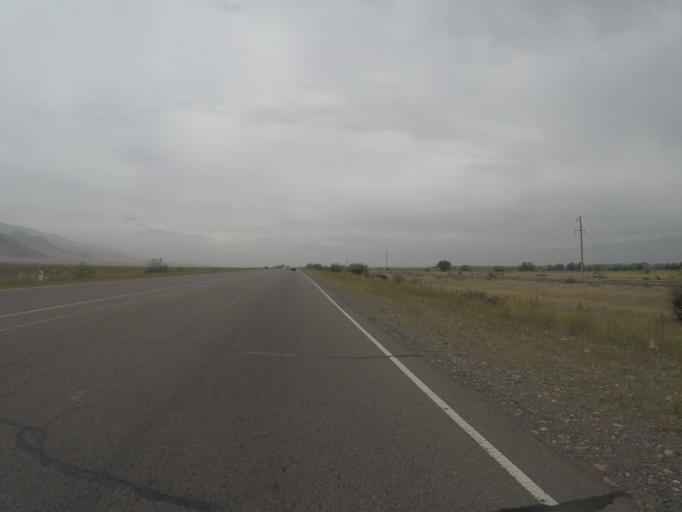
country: KG
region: Chuy
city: Tokmok
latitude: 42.8300
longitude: 75.4649
